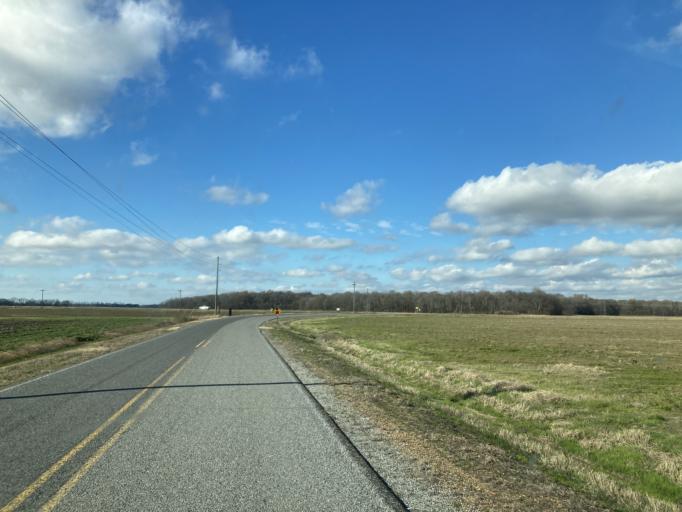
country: US
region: Mississippi
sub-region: Yazoo County
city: Yazoo City
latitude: 32.9602
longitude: -90.4878
